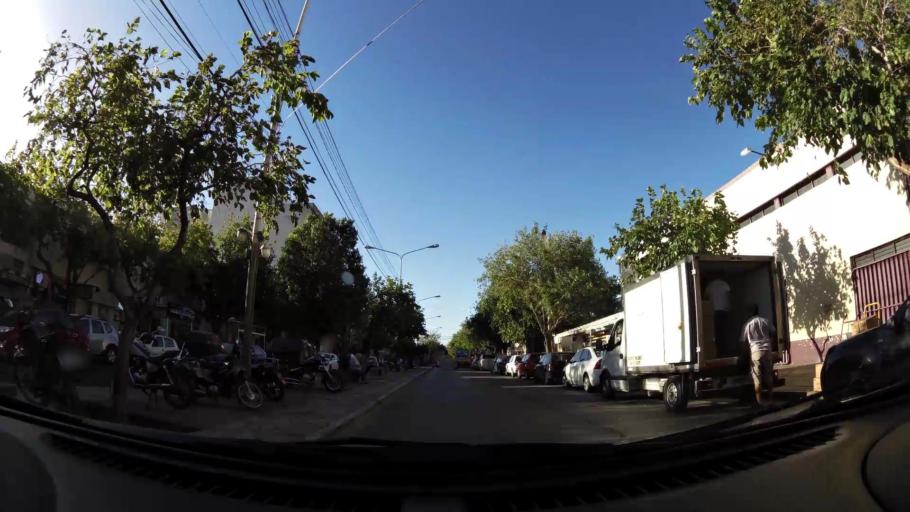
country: AR
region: San Juan
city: San Juan
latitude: -31.5350
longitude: -68.5216
